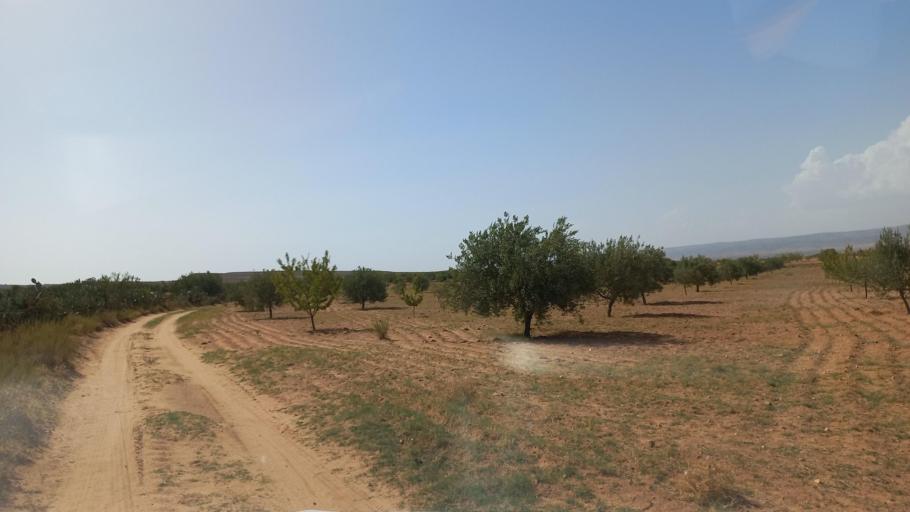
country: TN
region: Al Qasrayn
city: Kasserine
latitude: 35.2054
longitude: 9.0202
